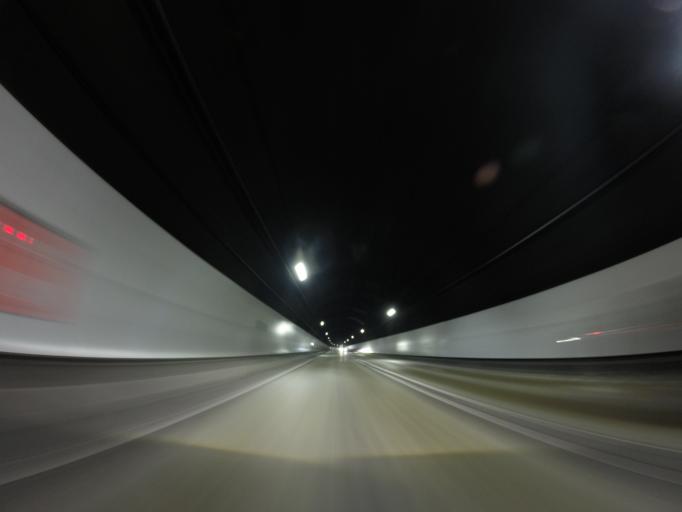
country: JP
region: Shizuoka
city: Mishima
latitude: 34.9811
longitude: 138.9363
